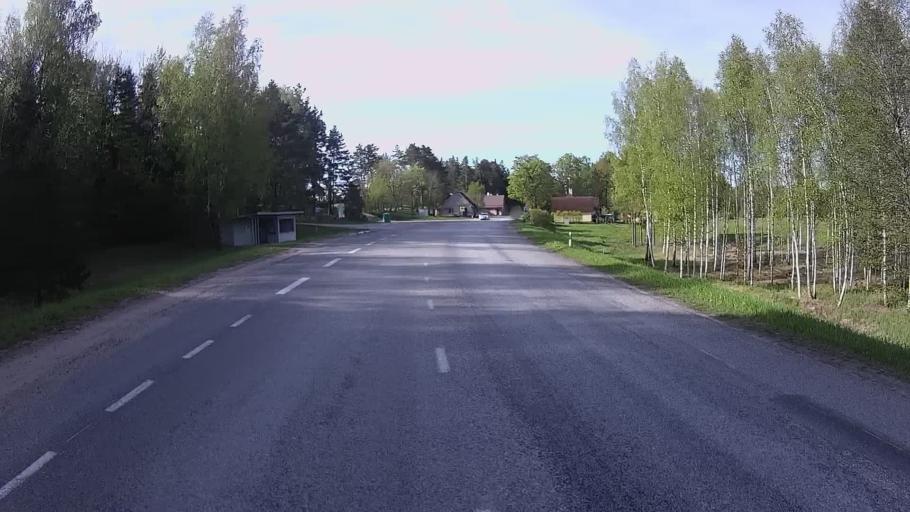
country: EE
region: Tartu
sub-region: Elva linn
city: Elva
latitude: 58.1273
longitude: 26.5222
